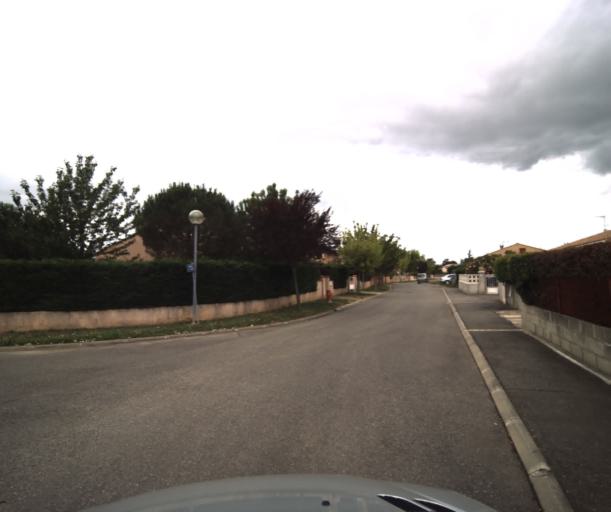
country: FR
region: Midi-Pyrenees
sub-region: Departement de la Haute-Garonne
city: Labarthe-sur-Leze
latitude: 43.4580
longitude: 1.4049
